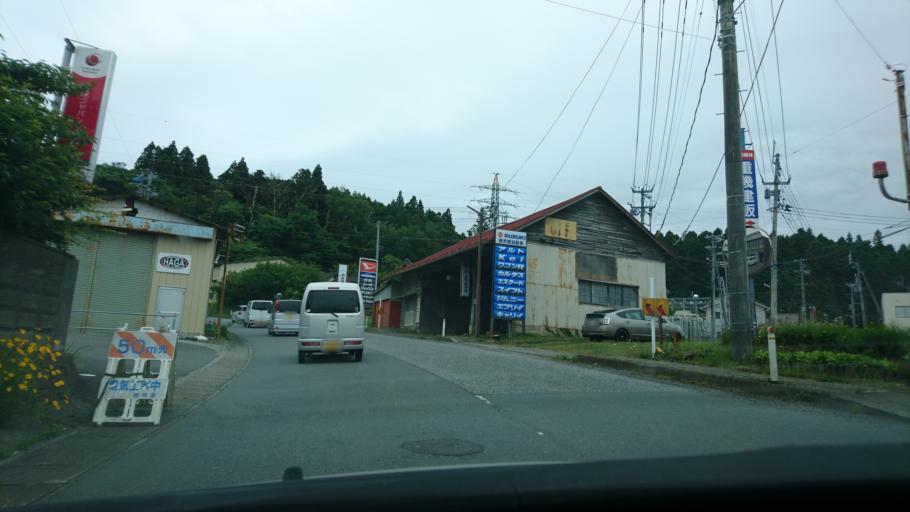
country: JP
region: Miyagi
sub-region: Oshika Gun
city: Onagawa Cho
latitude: 38.7882
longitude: 141.5056
